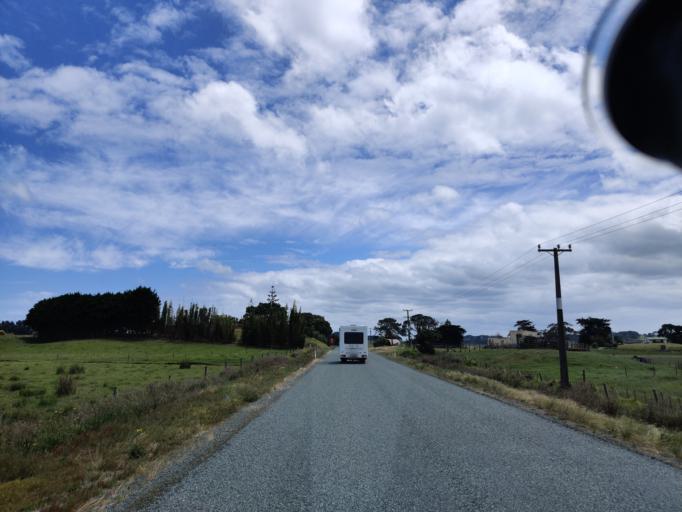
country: NZ
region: Northland
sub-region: Far North District
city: Kaitaia
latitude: -34.7746
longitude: 173.0913
